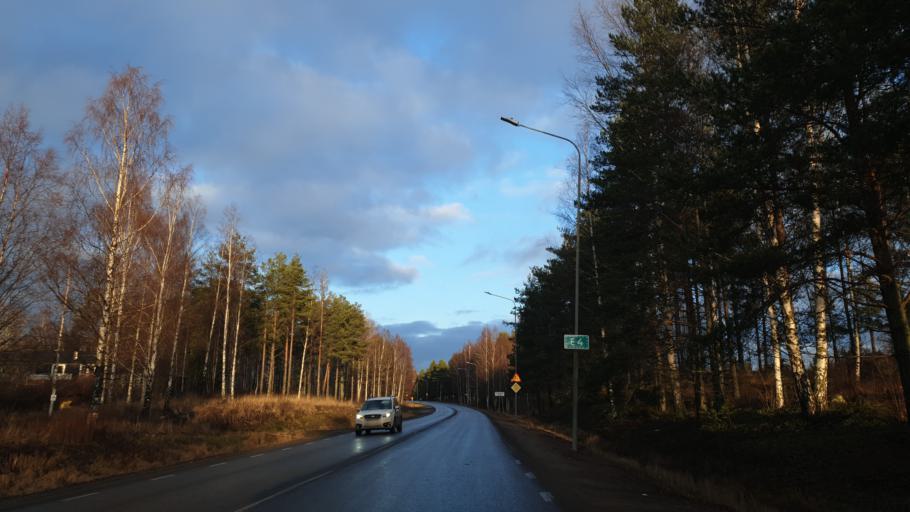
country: SE
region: Gaevleborg
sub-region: Hudiksvalls Kommun
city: Hudiksvall
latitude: 61.7245
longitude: 17.1449
